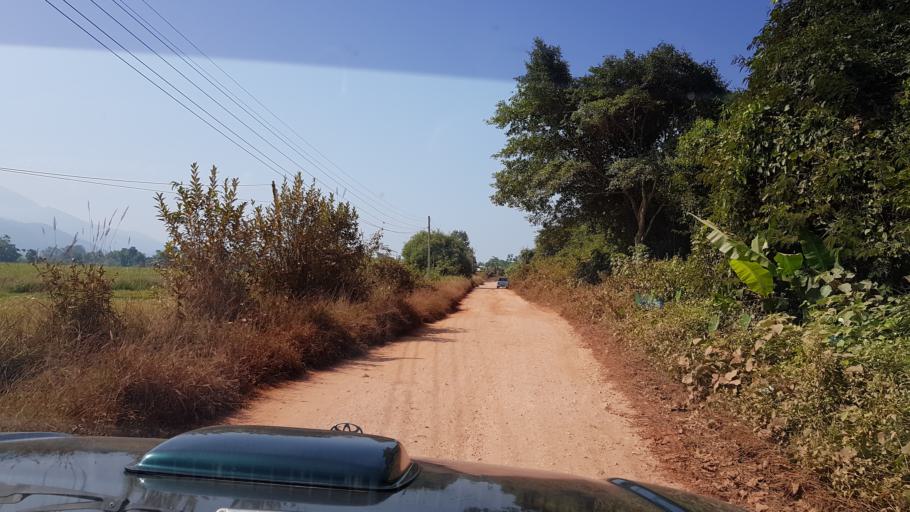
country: LA
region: Oudomxai
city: Muang Xay
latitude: 20.7115
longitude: 102.0355
